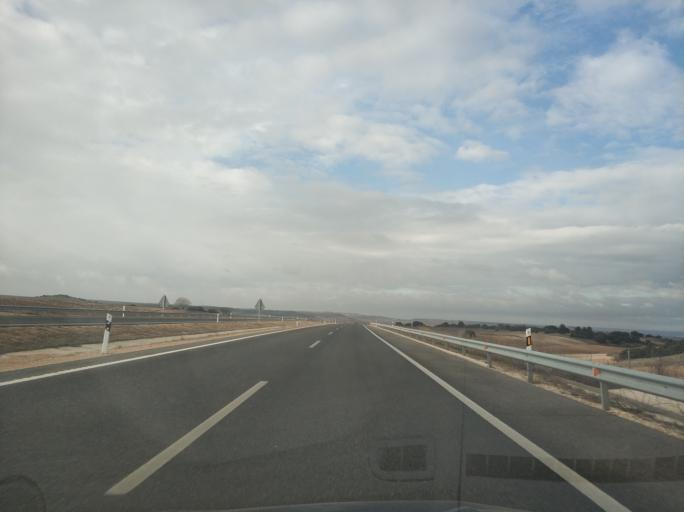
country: ES
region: Castille and Leon
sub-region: Provincia de Burgos
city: Campillo de Aranda
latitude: 41.6332
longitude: -3.7486
